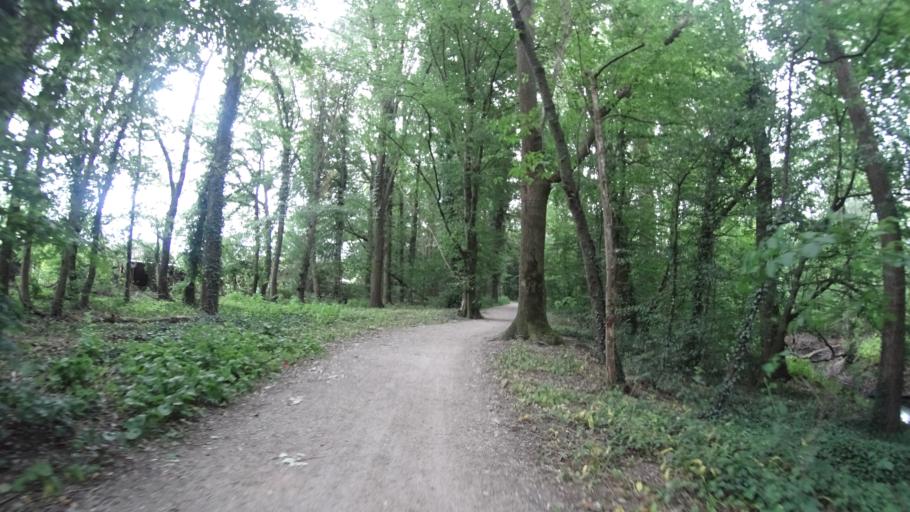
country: DE
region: Baden-Wuerttemberg
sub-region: Karlsruhe Region
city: Karlsruhe
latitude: 48.9827
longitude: 8.3868
